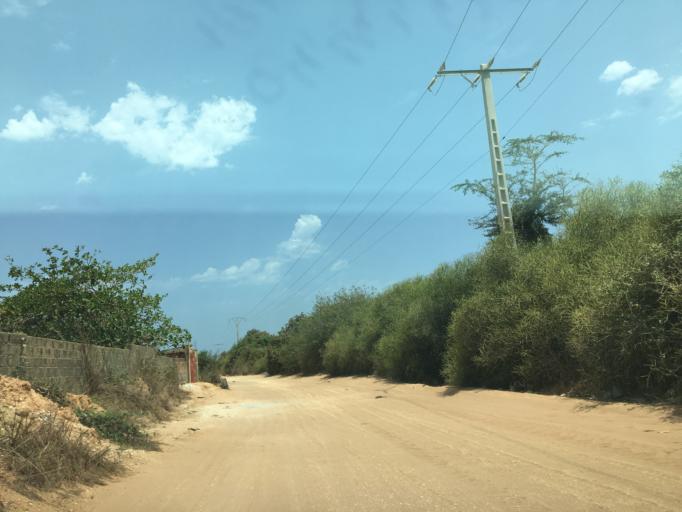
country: SN
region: Thies
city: Thies
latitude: 14.8147
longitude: -17.1940
